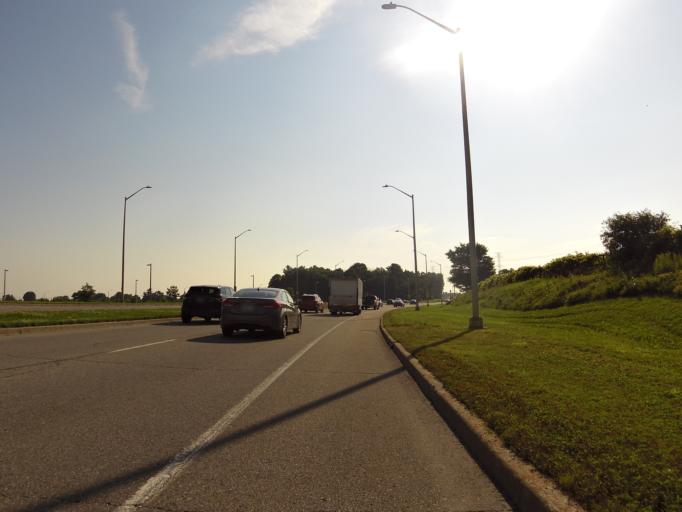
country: CA
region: Ontario
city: Bells Corners
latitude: 45.3227
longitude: -75.7750
